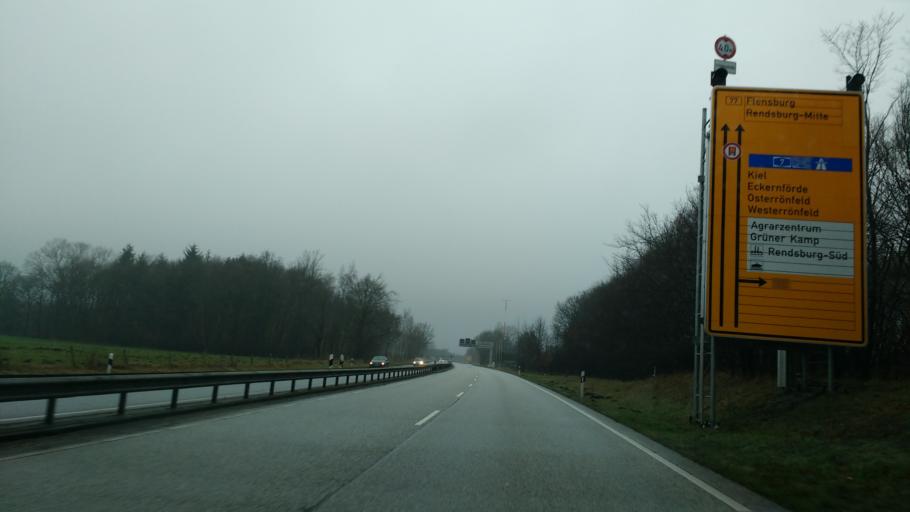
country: DE
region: Schleswig-Holstein
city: Westerronfeld
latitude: 54.2726
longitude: 9.6659
